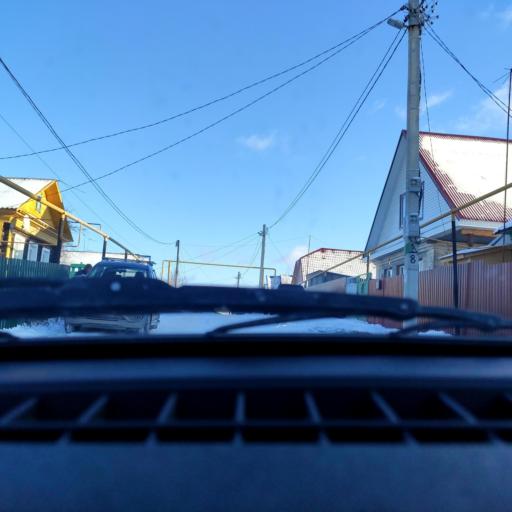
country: RU
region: Bashkortostan
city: Ufa
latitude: 54.8077
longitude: 56.1373
